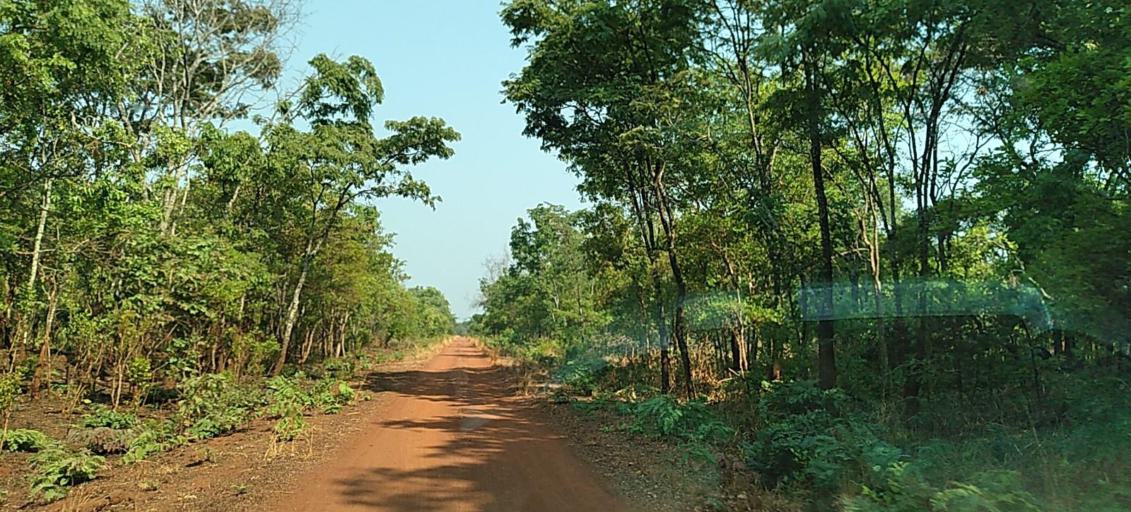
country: ZM
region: Copperbelt
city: Chingola
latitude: -12.8847
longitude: 27.4126
